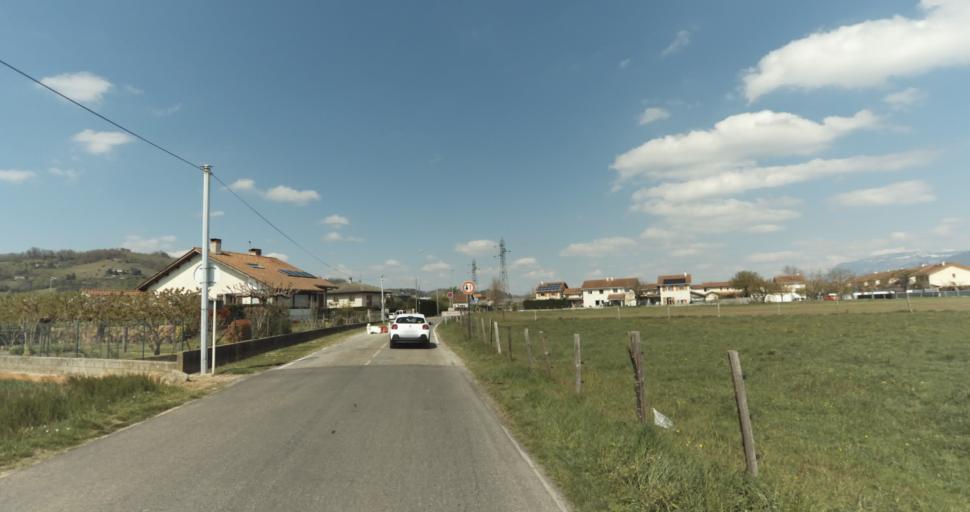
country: FR
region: Rhone-Alpes
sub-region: Departement de l'Isere
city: Saint-Marcellin
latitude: 45.1435
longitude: 5.3090
